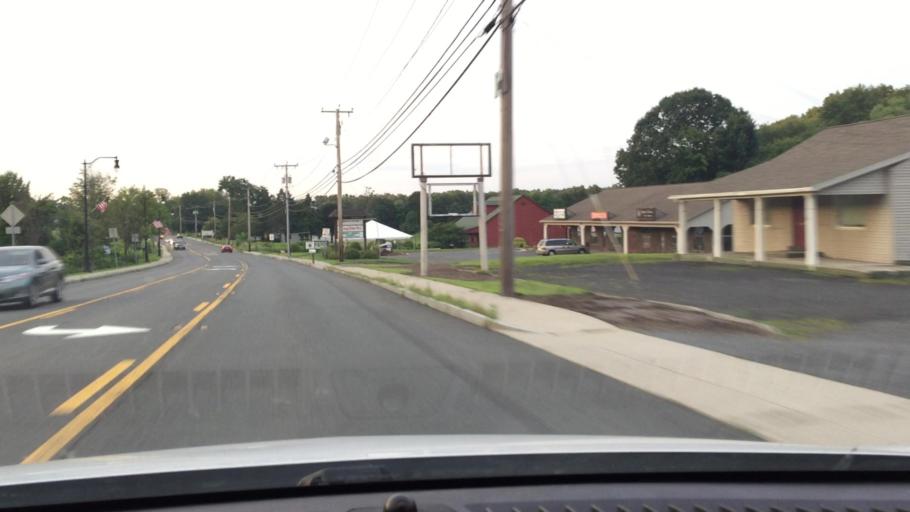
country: US
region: Massachusetts
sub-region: Hampden County
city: Southwick
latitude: 42.0612
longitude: -72.7623
